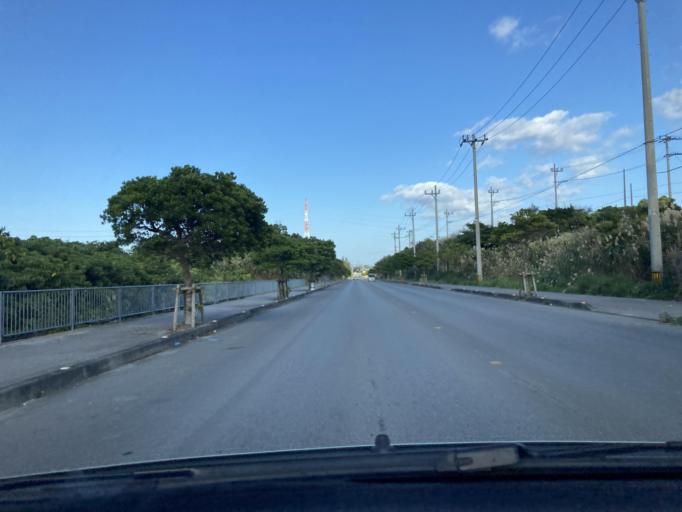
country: JP
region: Okinawa
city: Gushikawa
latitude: 26.3764
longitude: 127.8322
